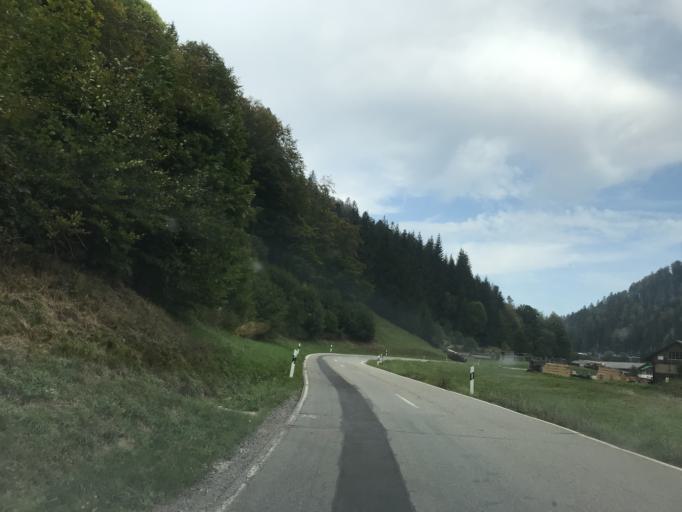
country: DE
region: Baden-Wuerttemberg
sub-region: Freiburg Region
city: Herrischried
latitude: 47.6985
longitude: 7.9829
